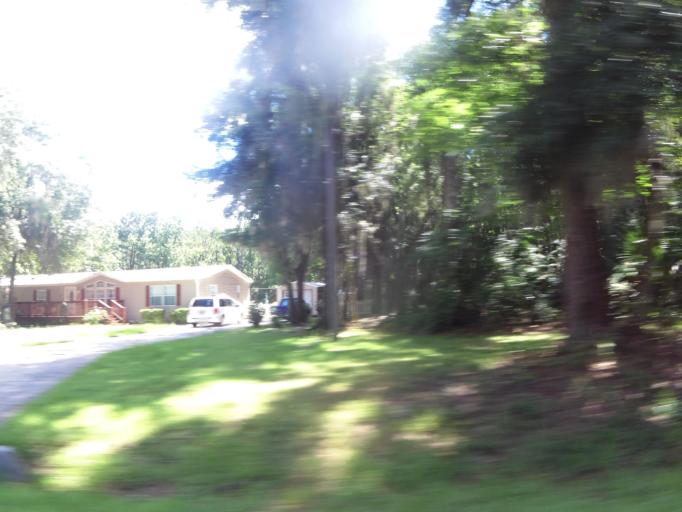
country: US
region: Georgia
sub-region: Camden County
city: St. Marys
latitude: 30.6795
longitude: -81.5340
